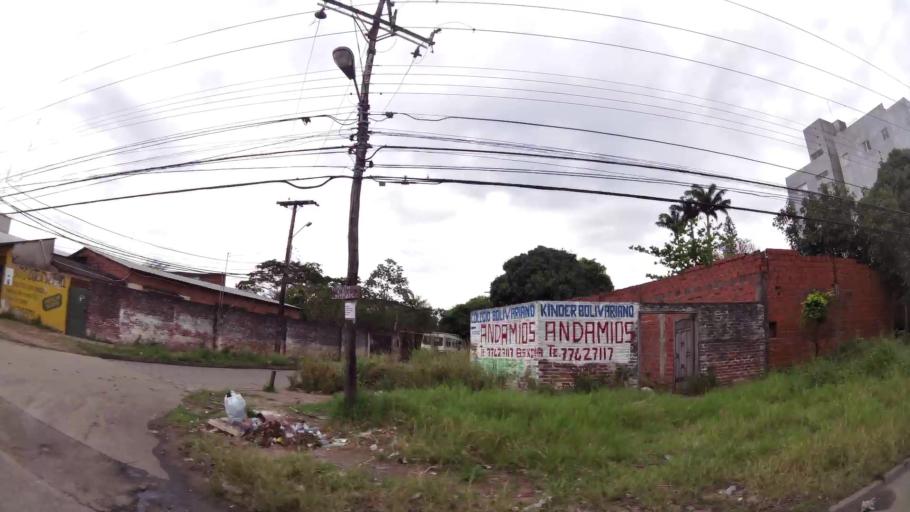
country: BO
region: Santa Cruz
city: Santa Cruz de la Sierra
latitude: -17.7579
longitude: -63.1769
